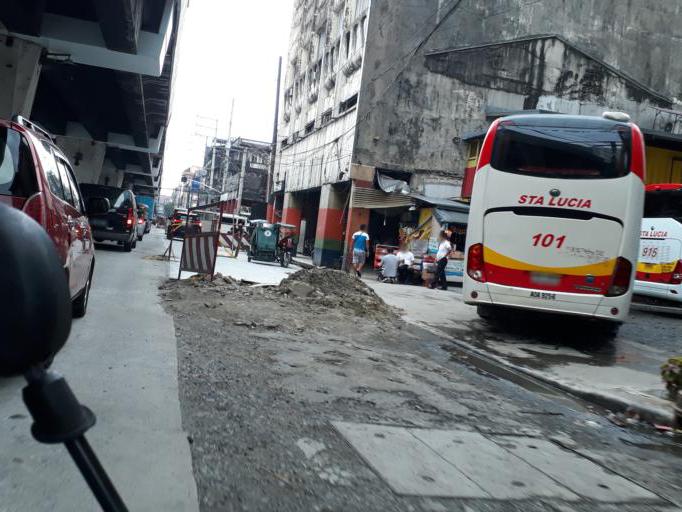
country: PH
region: Metro Manila
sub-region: City of Manila
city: Manila
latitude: 14.6067
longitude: 120.9822
